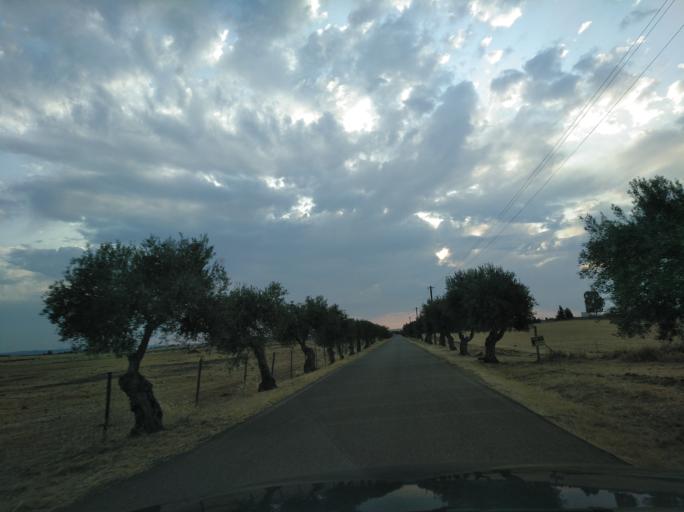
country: PT
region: Portalegre
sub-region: Campo Maior
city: Campo Maior
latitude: 39.0166
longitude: -7.0407
